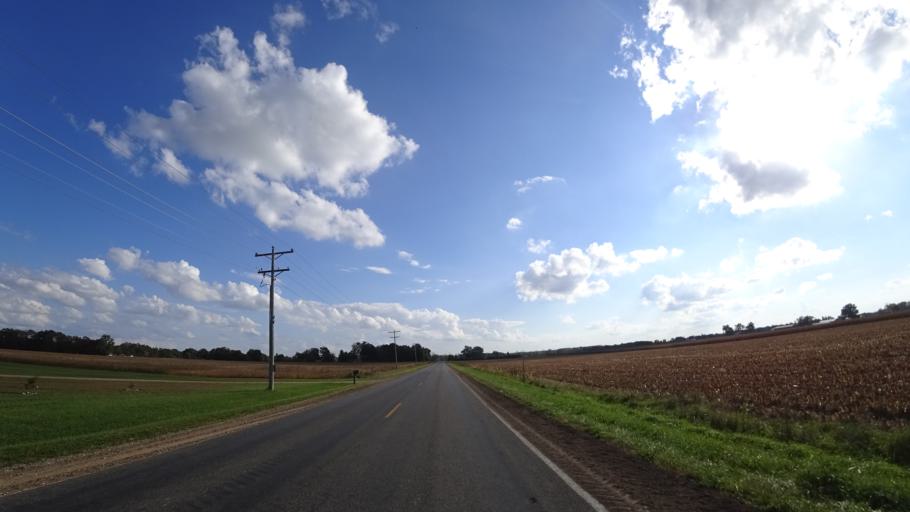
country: US
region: Michigan
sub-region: Saint Joseph County
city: Centreville
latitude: 41.9449
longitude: -85.5277
